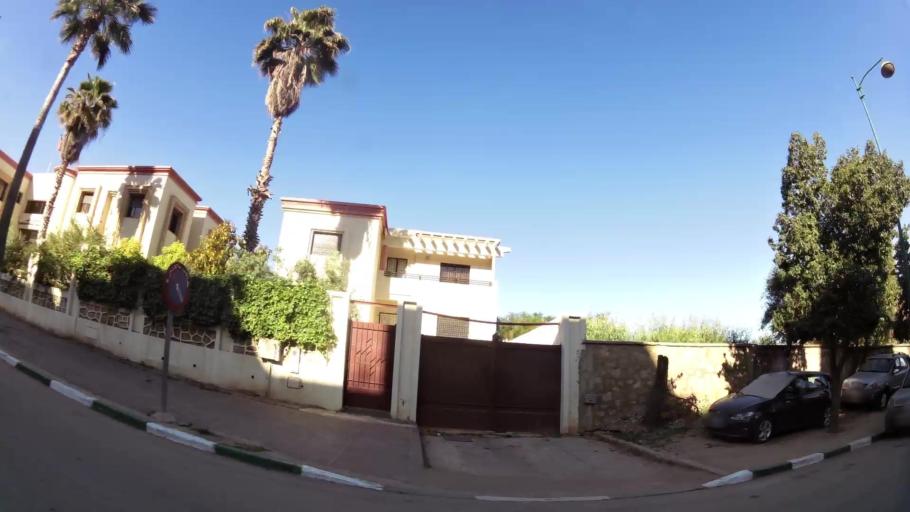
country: MA
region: Meknes-Tafilalet
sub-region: Meknes
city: Meknes
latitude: 33.8692
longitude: -5.5764
